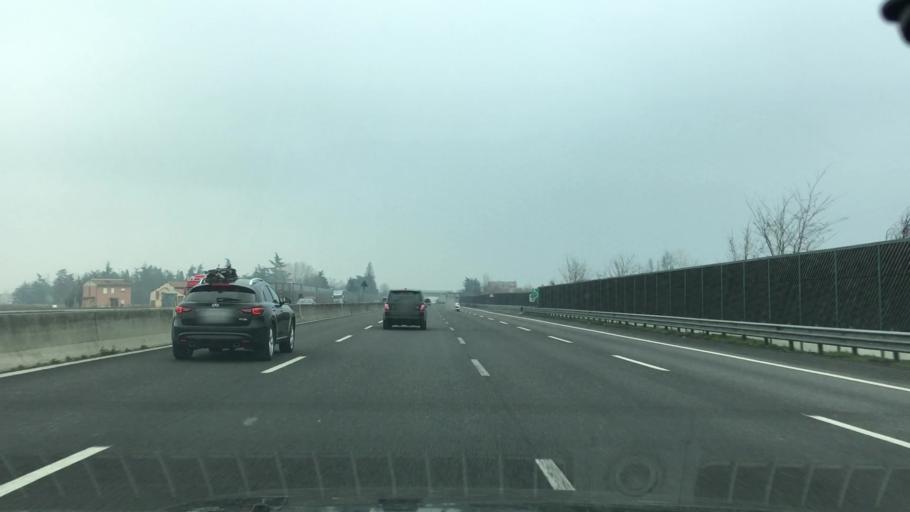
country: IT
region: Emilia-Romagna
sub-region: Provincia di Modena
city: San Cesario sul Panaro
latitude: 44.5680
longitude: 11.0289
